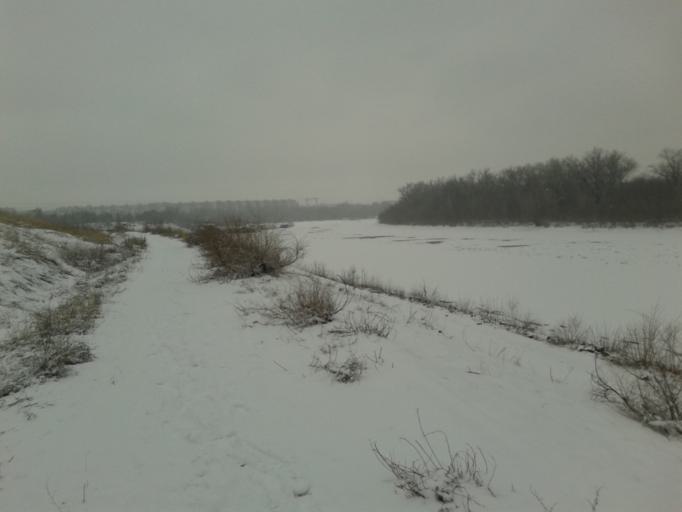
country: RU
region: Volgograd
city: Krasnoslobodsk
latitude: 48.5271
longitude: 44.5562
